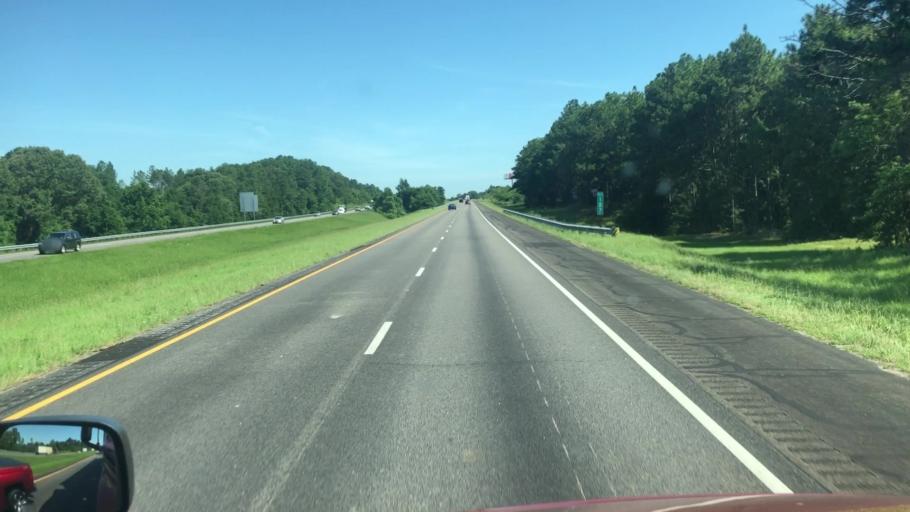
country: US
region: Alabama
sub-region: Autauga County
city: Pine Level
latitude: 32.5570
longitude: -86.4620
